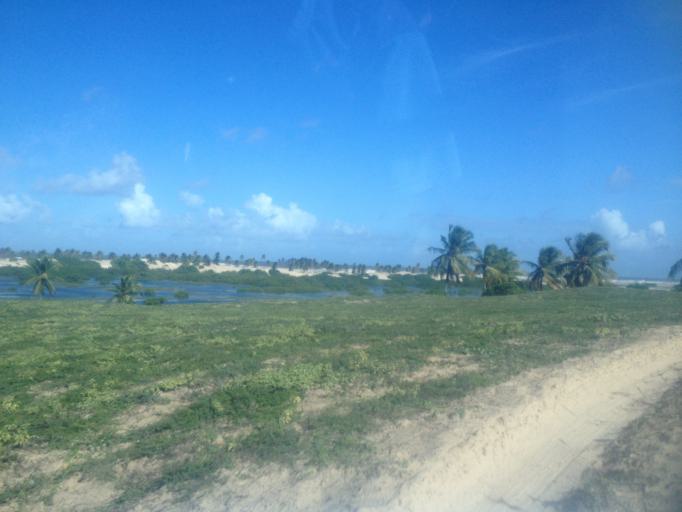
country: BR
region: Sergipe
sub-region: Indiaroba
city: Indiaroba
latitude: -11.4694
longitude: -37.3673
